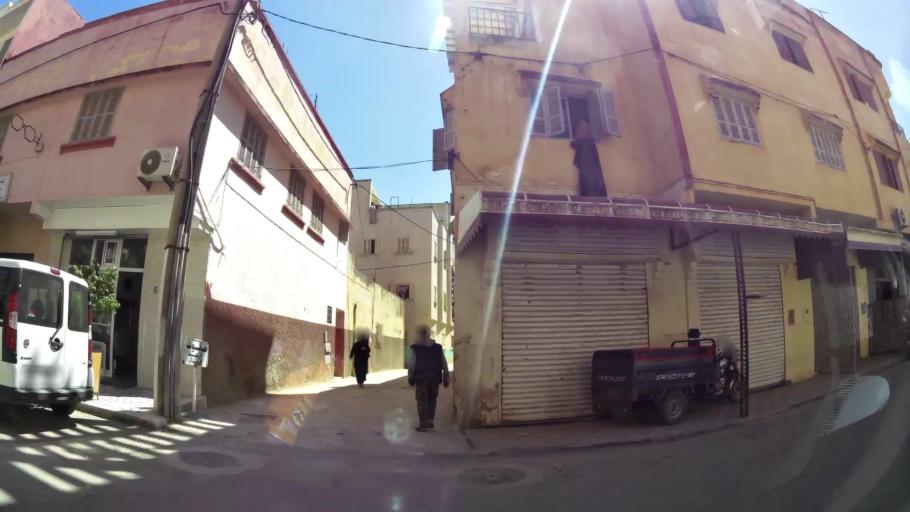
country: MA
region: Meknes-Tafilalet
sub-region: Meknes
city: Meknes
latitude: 33.8672
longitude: -5.5483
